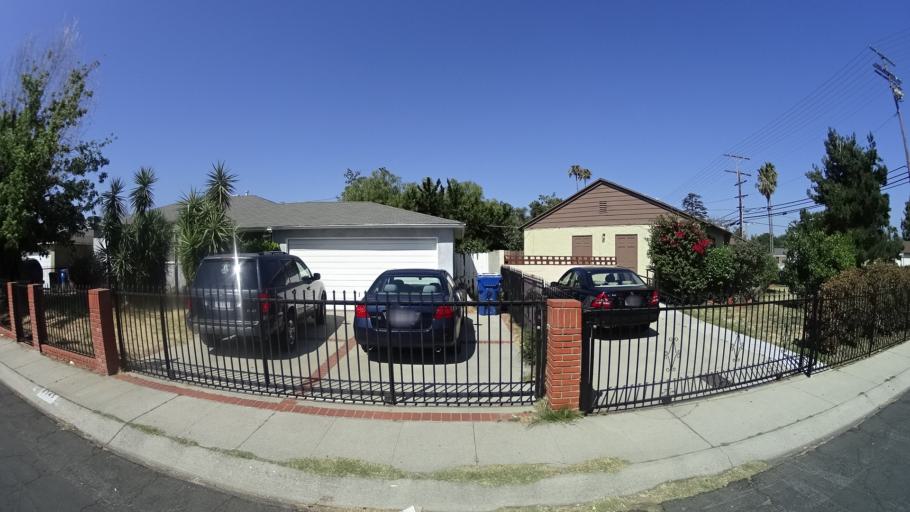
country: US
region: California
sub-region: Los Angeles County
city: Van Nuys
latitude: 34.2290
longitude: -118.4461
